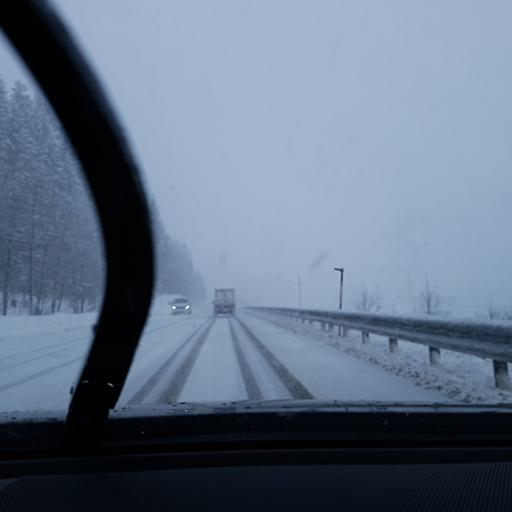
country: AT
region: Salzburg
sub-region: Politischer Bezirk Hallein
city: Abtenau
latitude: 47.5820
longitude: 13.4507
